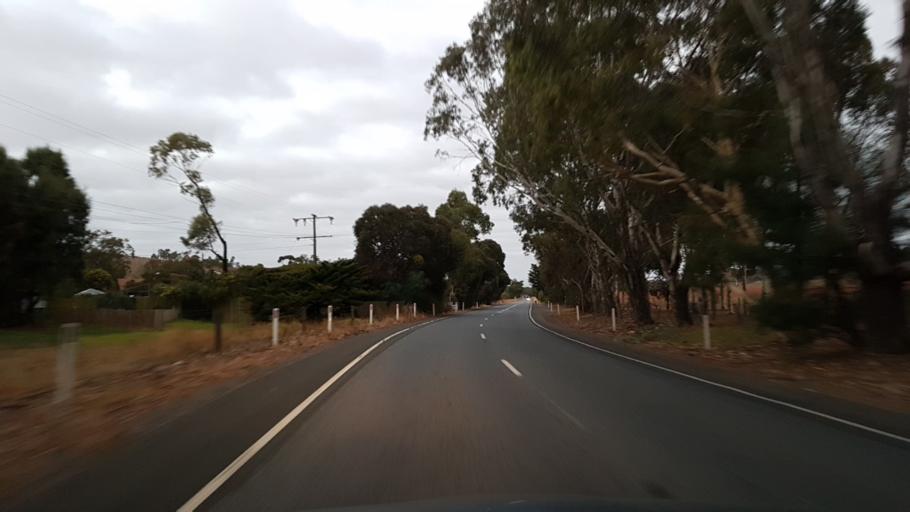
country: AU
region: South Australia
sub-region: Mount Barker
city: Callington
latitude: -35.0591
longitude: 139.0116
